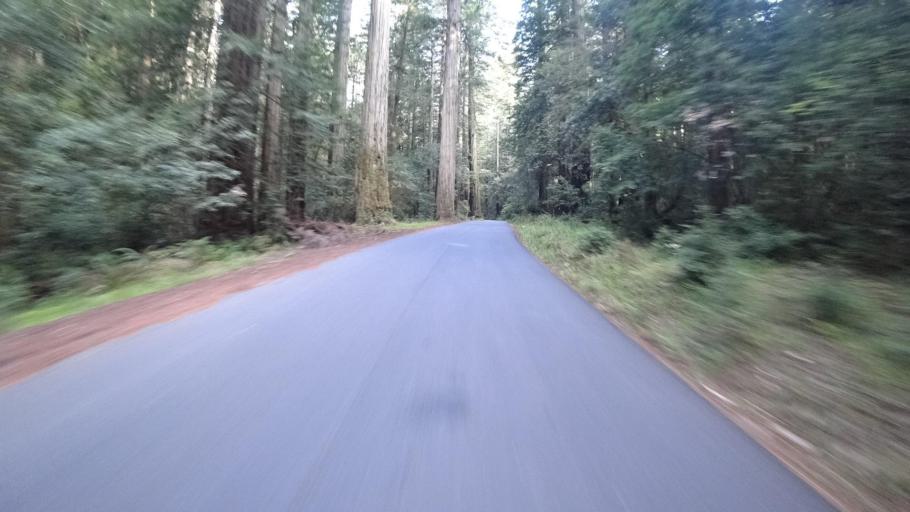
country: US
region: California
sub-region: Humboldt County
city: Rio Dell
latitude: 40.3487
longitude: -123.9587
